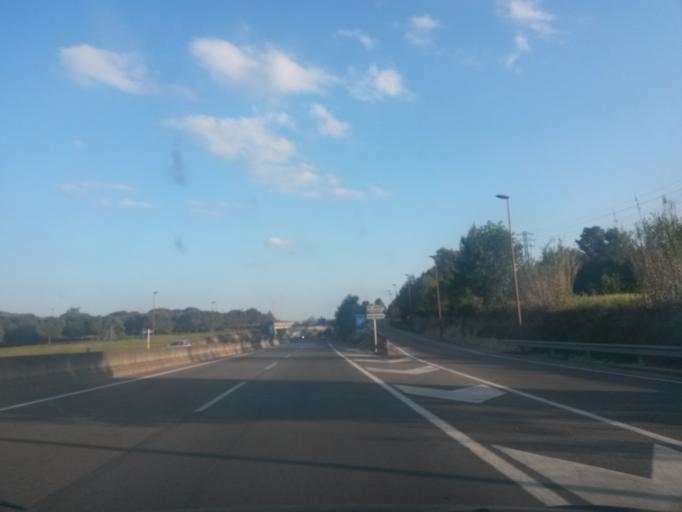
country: ES
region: Catalonia
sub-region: Provincia de Girona
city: Sarria de Ter
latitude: 42.0380
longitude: 2.8230
